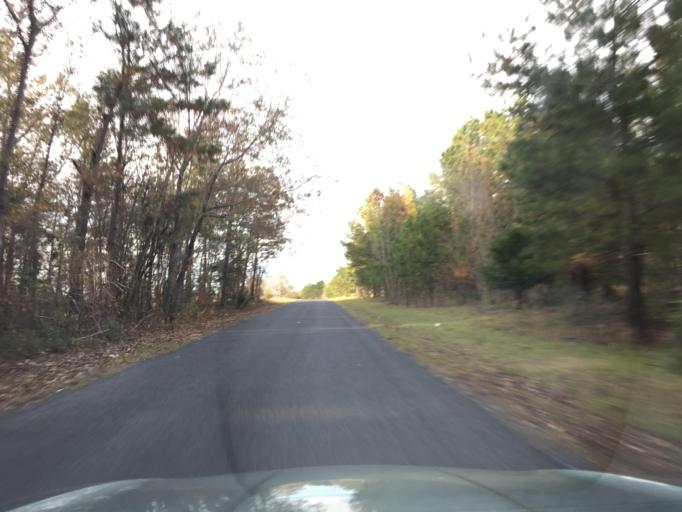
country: US
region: South Carolina
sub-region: Lexington County
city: Leesville
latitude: 33.6782
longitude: -81.3751
